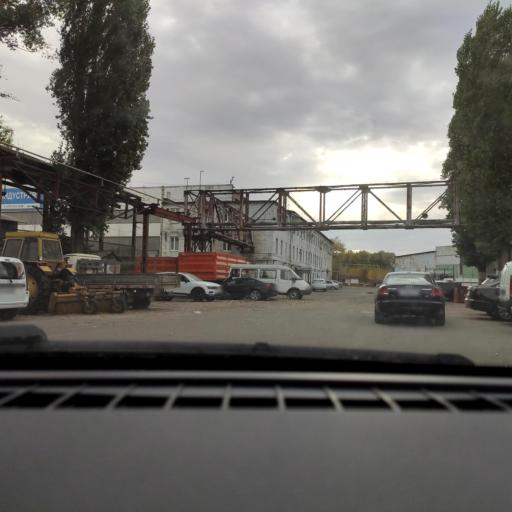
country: RU
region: Voronezj
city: Voronezh
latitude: 51.6572
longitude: 39.2823
